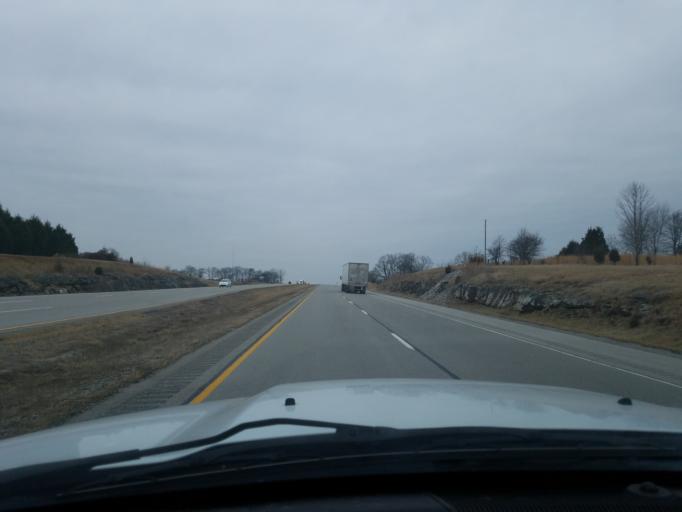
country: US
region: Kentucky
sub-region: Logan County
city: Auburn
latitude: 36.8922
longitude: -86.6190
